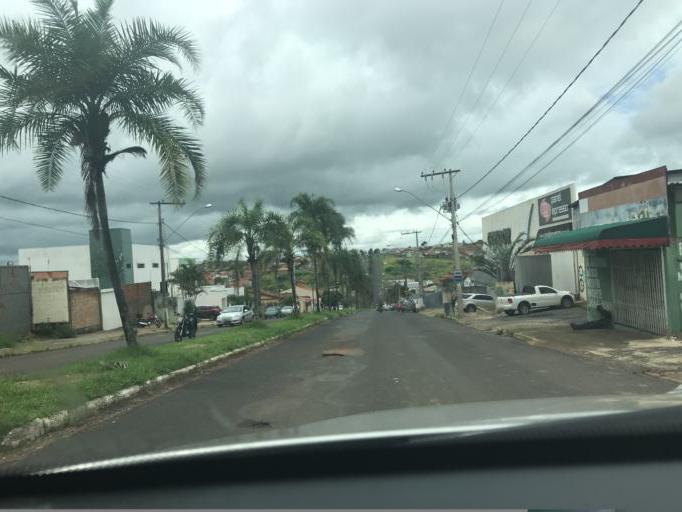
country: BR
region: Minas Gerais
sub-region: Araxa
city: Araxa
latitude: -19.5800
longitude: -46.9346
